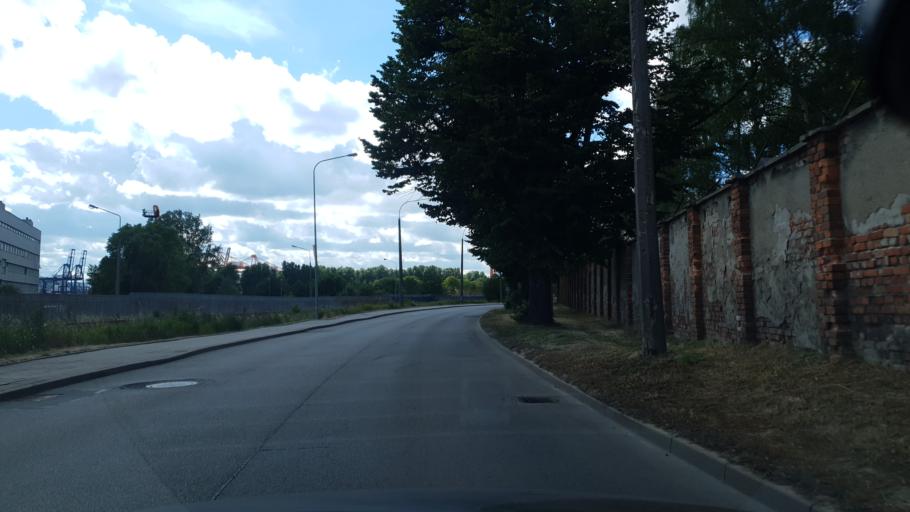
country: PL
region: Pomeranian Voivodeship
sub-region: Gdynia
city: Gdynia
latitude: 54.5432
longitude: 18.5292
